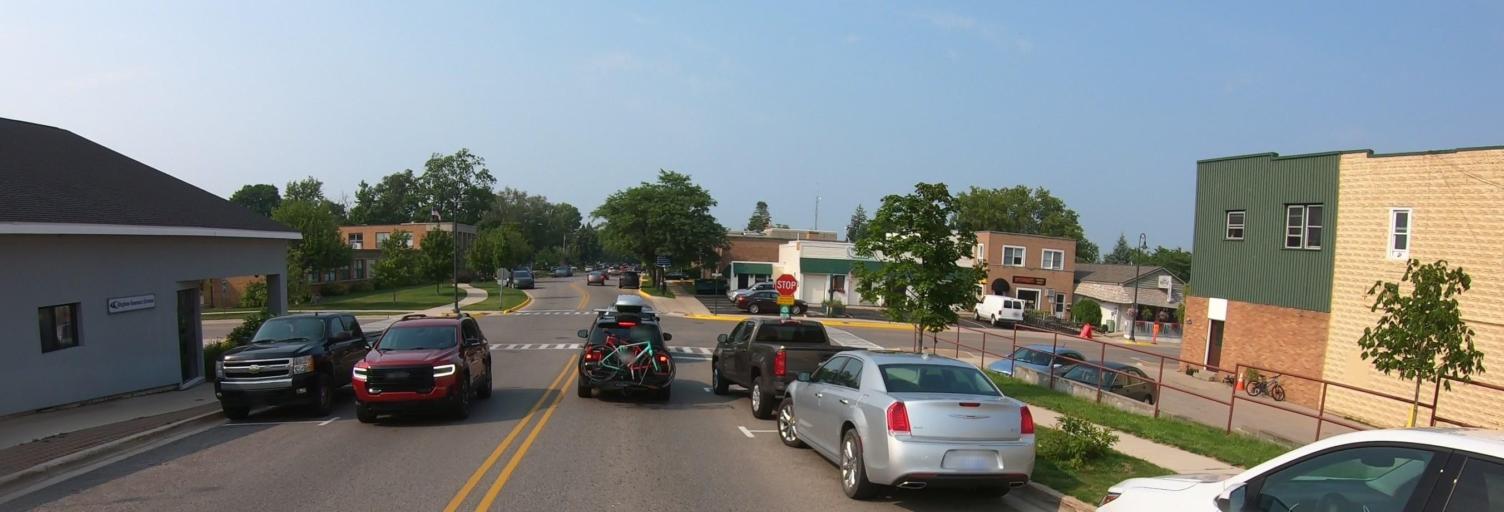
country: US
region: Michigan
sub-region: Charlevoix County
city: Charlevoix
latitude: 45.3150
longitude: -85.2606
